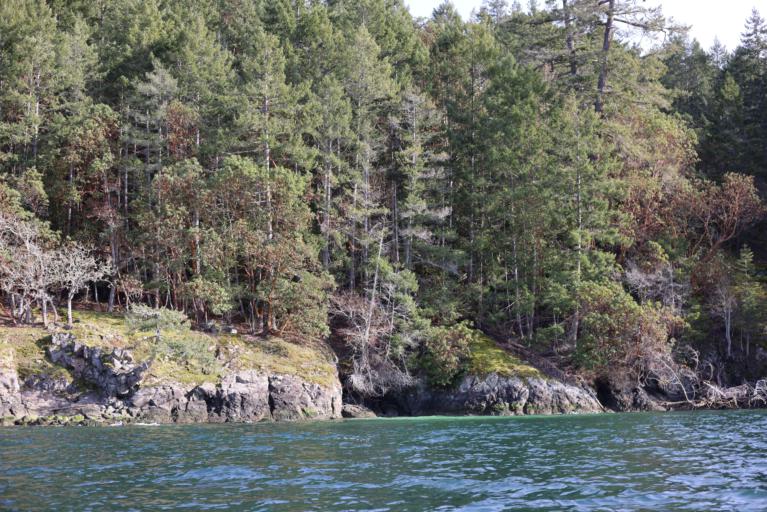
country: CA
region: British Columbia
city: Duncan
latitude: 48.7475
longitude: -123.5787
